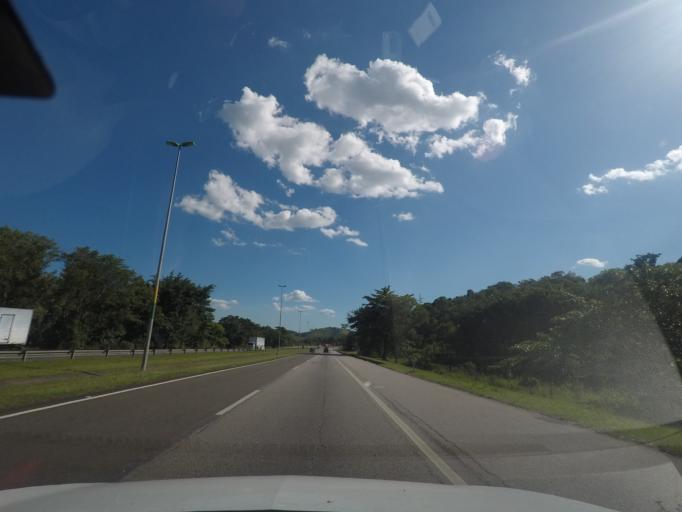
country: BR
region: Rio de Janeiro
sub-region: Guapimirim
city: Guapimirim
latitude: -22.5983
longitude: -43.0246
